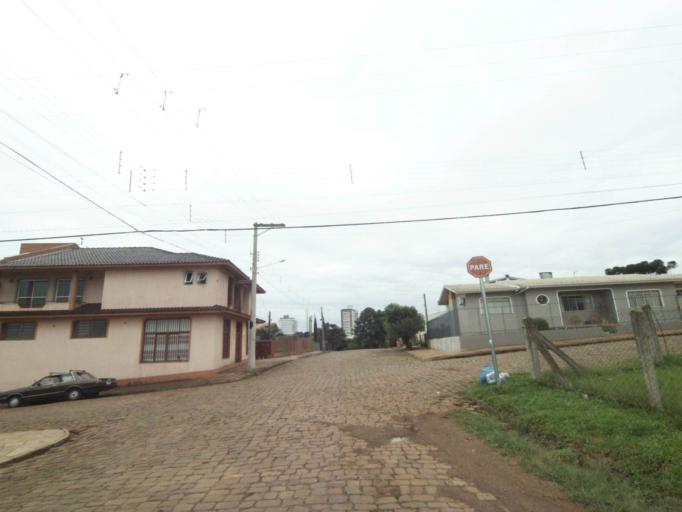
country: BR
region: Rio Grande do Sul
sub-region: Lagoa Vermelha
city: Lagoa Vermelha
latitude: -28.2173
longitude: -51.5204
